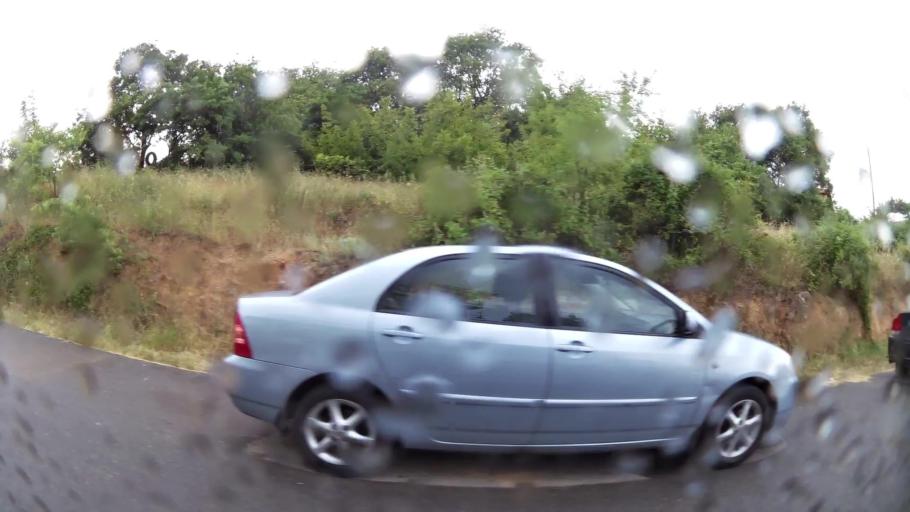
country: GR
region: Central Macedonia
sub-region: Nomos Imathias
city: Veroia
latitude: 40.5215
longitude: 22.1932
